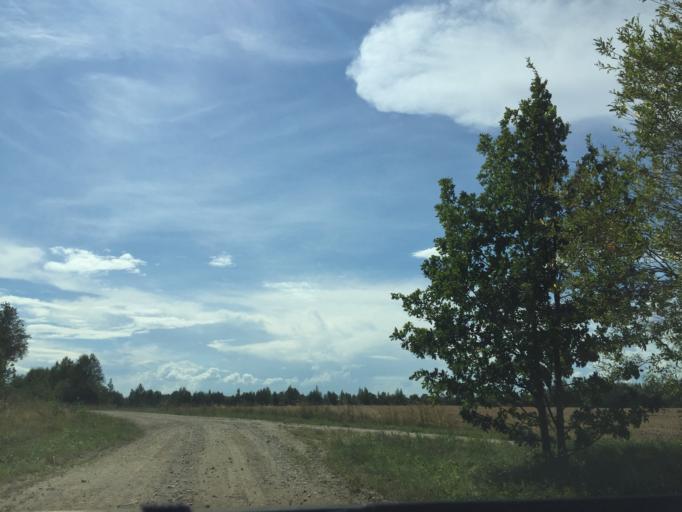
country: LT
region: Siauliu apskritis
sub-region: Joniskis
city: Joniskis
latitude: 56.3008
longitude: 23.6459
